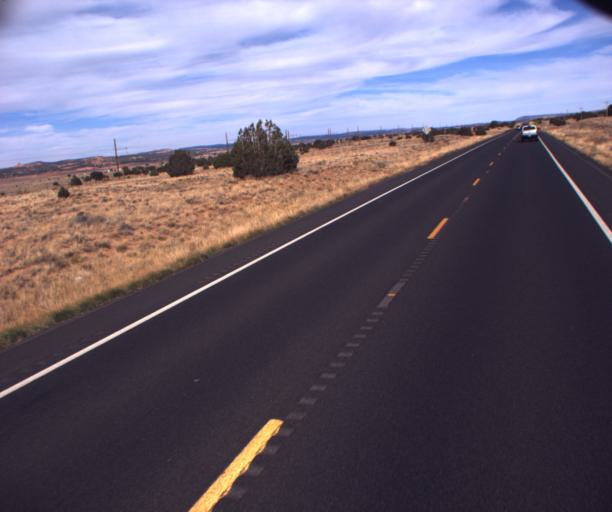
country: US
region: Arizona
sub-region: Navajo County
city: Kayenta
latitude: 36.4905
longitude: -110.6327
